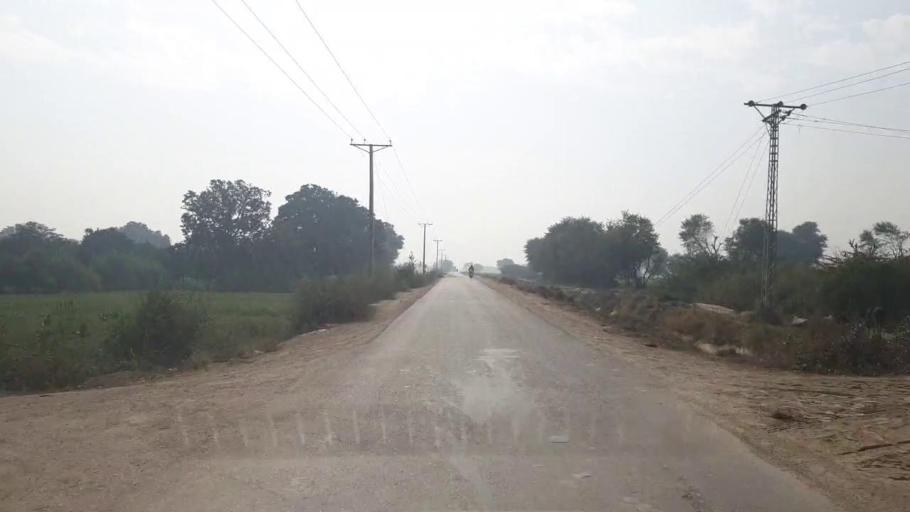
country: PK
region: Sindh
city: Hala
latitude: 25.7911
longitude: 68.4402
